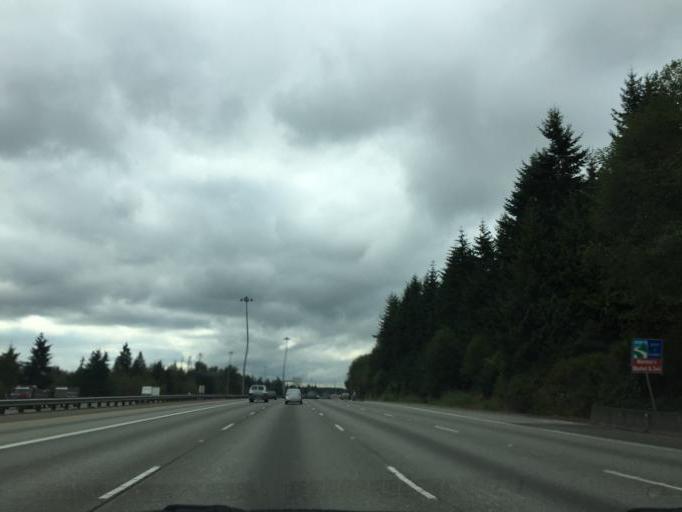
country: US
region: Washington
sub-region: King County
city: Federal Way
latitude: 47.3247
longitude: -122.2946
